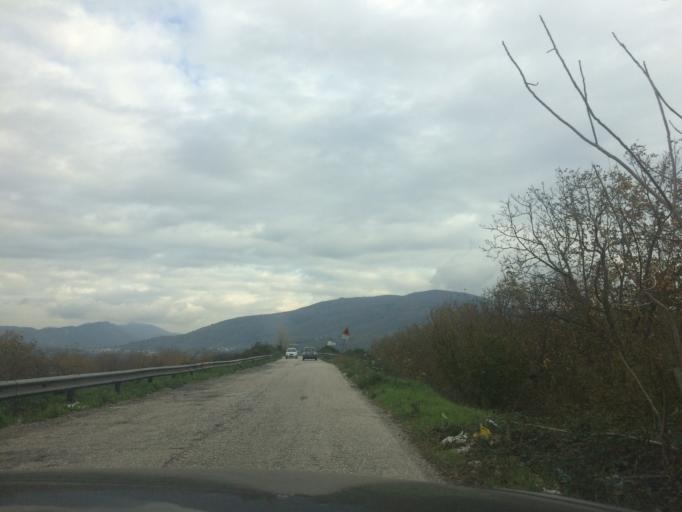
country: IT
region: Campania
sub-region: Provincia di Napoli
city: San Gennaro Vesuviano
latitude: 40.8736
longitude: 14.5321
